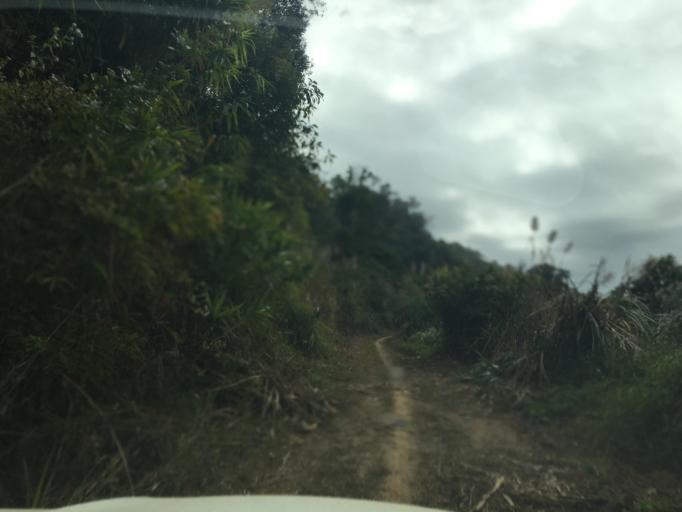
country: LA
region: Houaphan
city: Viengthong
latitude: 19.9282
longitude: 103.2956
